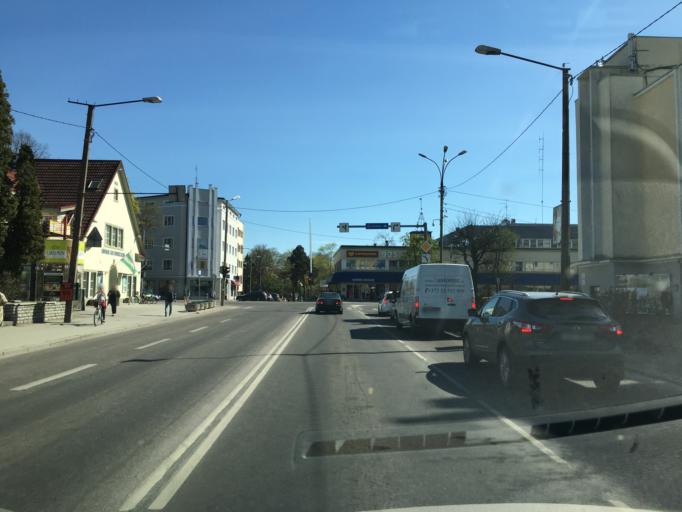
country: EE
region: Harju
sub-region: Saue vald
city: Laagri
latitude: 59.3885
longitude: 24.6834
